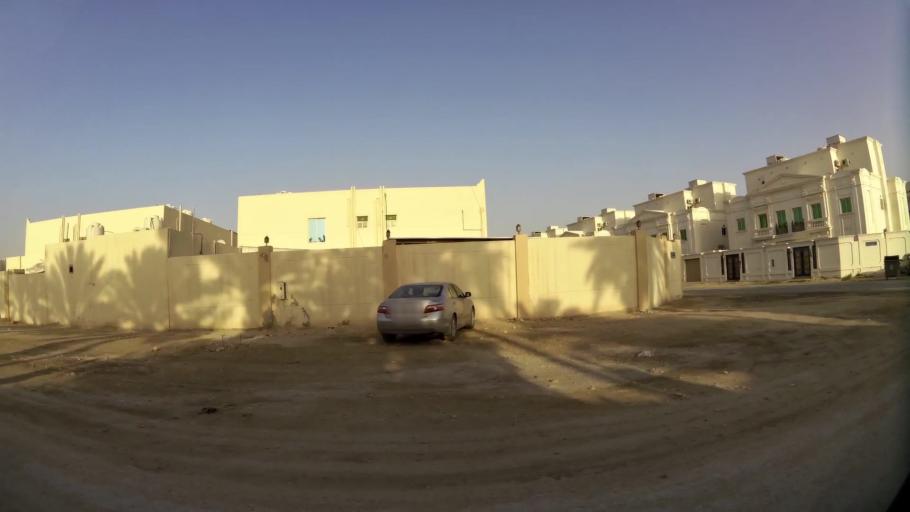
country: QA
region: Baladiyat ar Rayyan
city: Ar Rayyan
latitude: 25.3219
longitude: 51.4528
